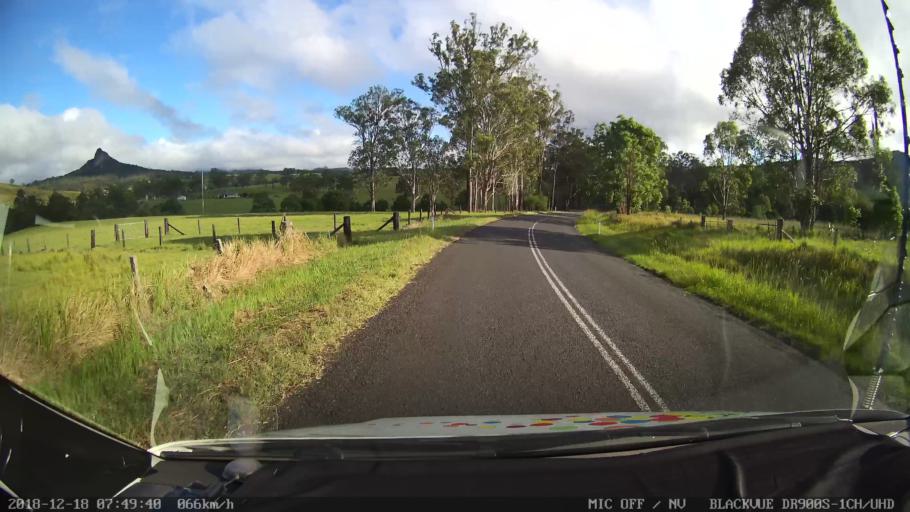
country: AU
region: New South Wales
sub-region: Kyogle
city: Kyogle
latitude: -28.4519
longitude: 152.5703
